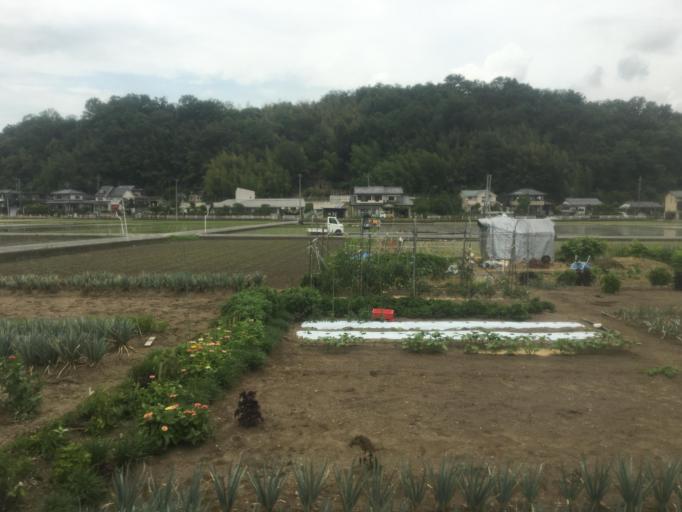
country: JP
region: Gunma
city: Fujioka
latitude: 36.2751
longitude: 139.0374
